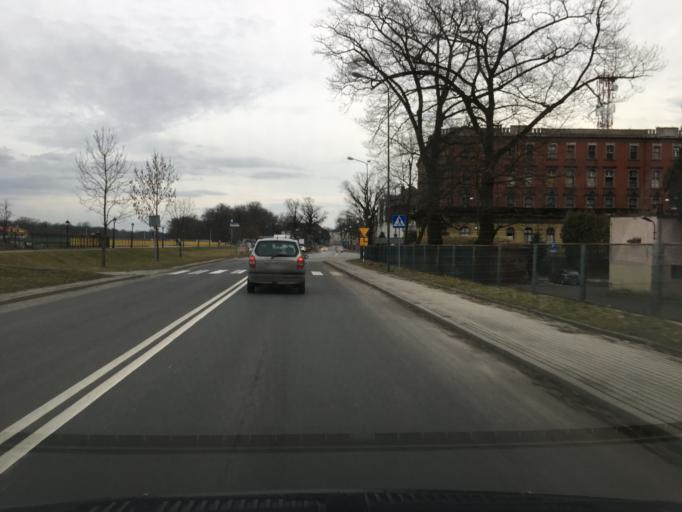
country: PL
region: Opole Voivodeship
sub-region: Powiat kedzierzynsko-kozielski
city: Kozle
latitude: 50.3378
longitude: 18.1442
